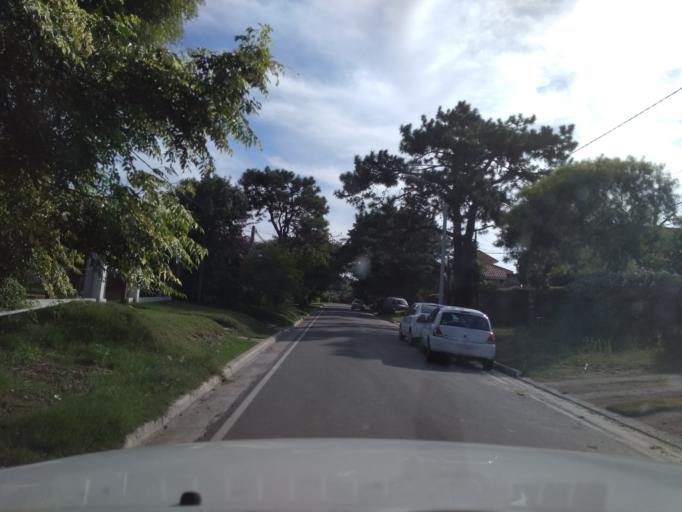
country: UY
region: Canelones
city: Barra de Carrasco
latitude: -34.8704
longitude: -56.0371
